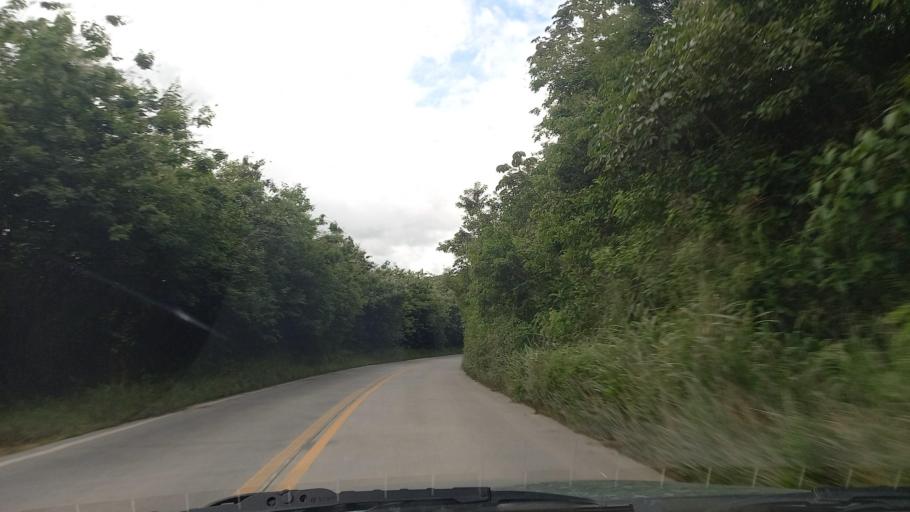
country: BR
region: Pernambuco
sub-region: Quipapa
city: Quipapa
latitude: -8.7826
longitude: -35.9498
